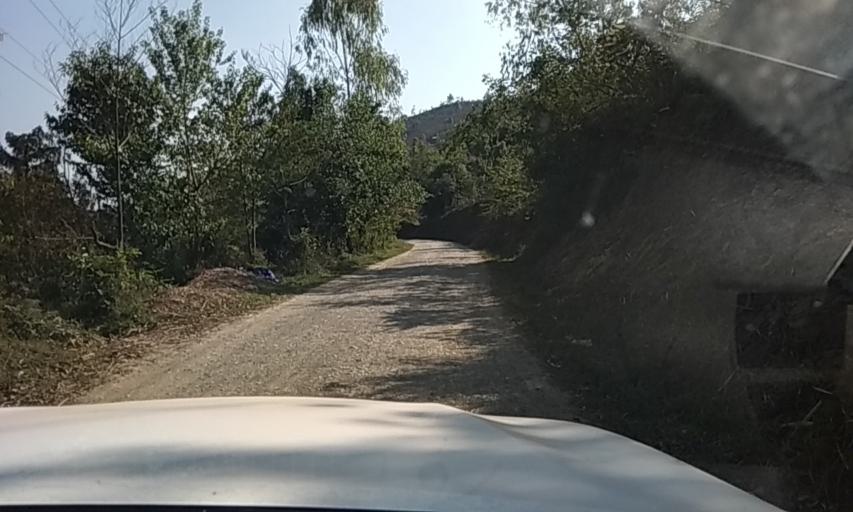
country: LA
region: Phongsali
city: Phongsali
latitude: 21.6556
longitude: 102.0909
